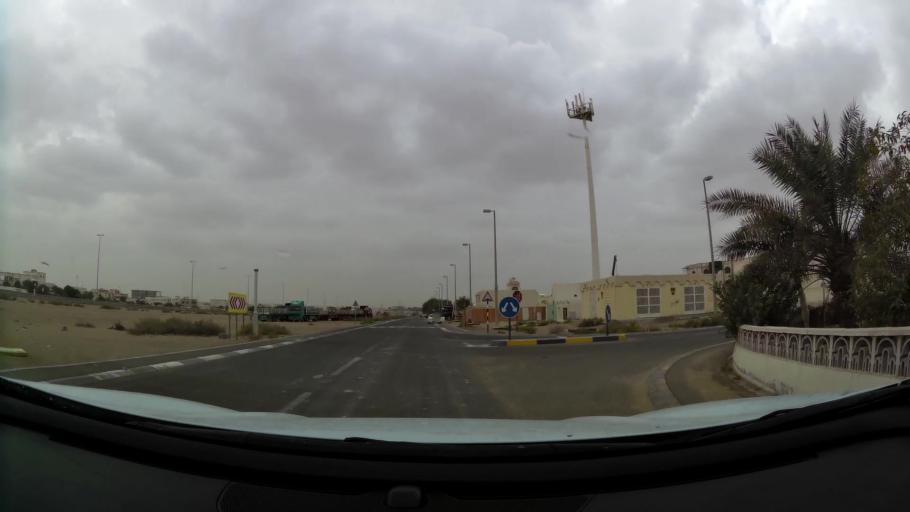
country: AE
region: Abu Dhabi
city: Abu Dhabi
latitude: 24.3329
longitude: 54.6398
